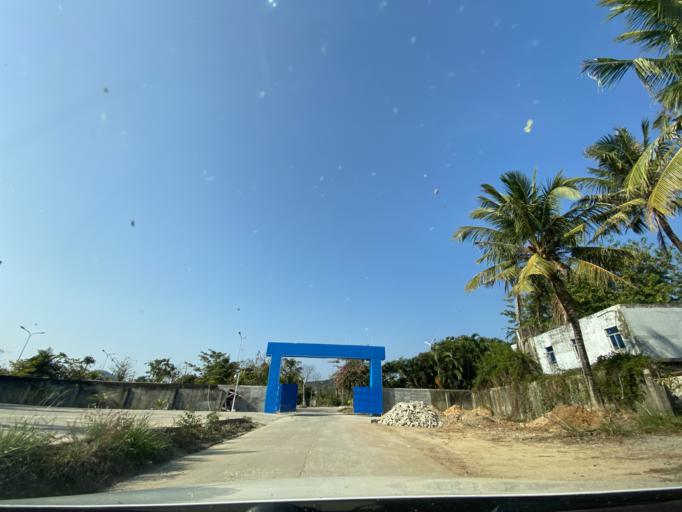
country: CN
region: Hainan
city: Haitangwan
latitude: 18.4025
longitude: 109.7656
